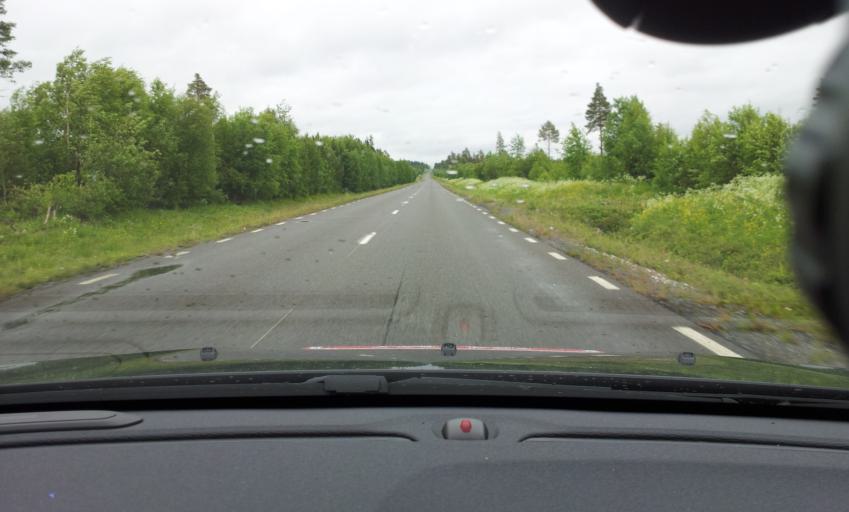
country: SE
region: Jaemtland
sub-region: OEstersunds Kommun
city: Lit
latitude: 63.7272
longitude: 14.9265
